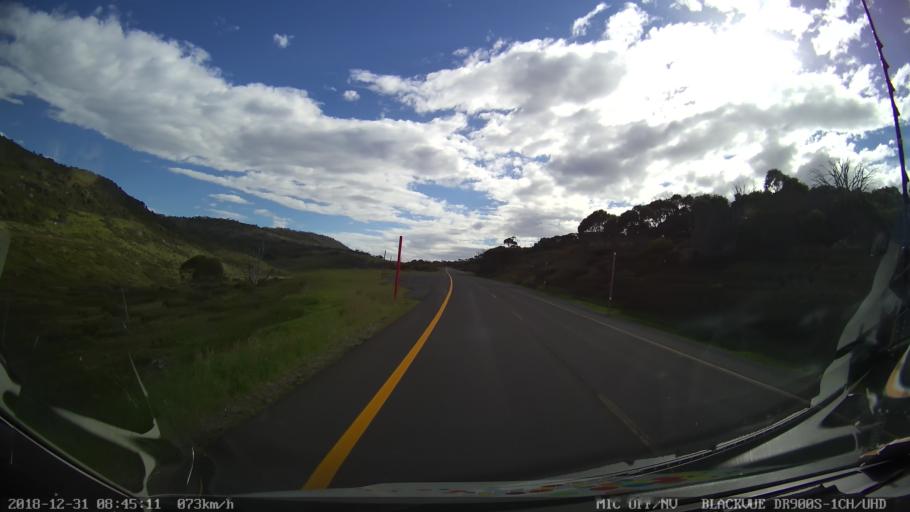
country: AU
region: New South Wales
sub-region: Snowy River
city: Jindabyne
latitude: -36.3783
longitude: 148.4625
